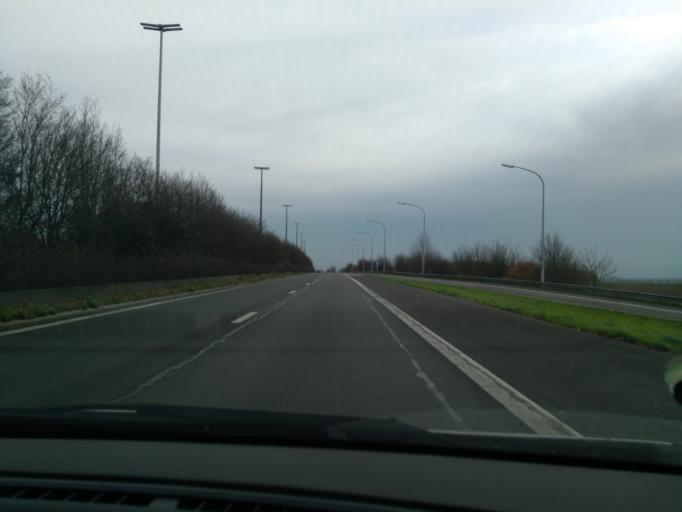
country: BE
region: Wallonia
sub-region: Province du Hainaut
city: Antoing
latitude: 50.5521
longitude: 3.5148
